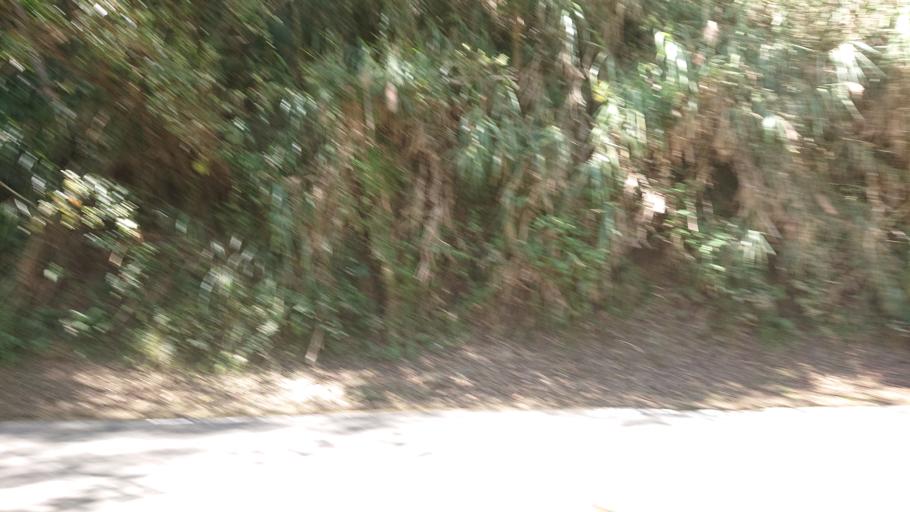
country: TW
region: Taiwan
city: Lugu
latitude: 23.4819
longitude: 120.8549
